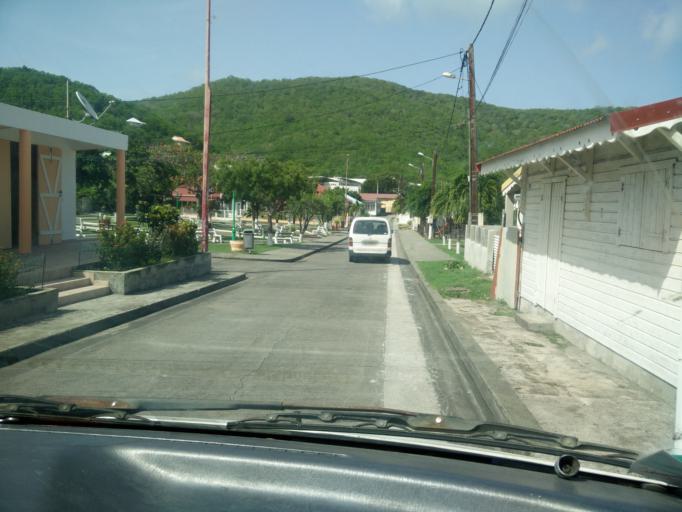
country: GP
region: Guadeloupe
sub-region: Guadeloupe
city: Terre-de-Bas
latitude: 15.8489
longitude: -61.6437
